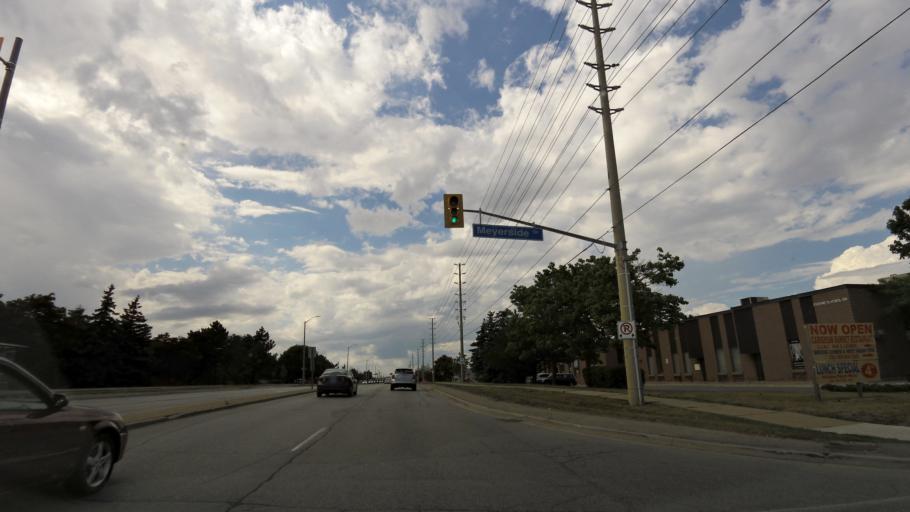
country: CA
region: Ontario
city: Mississauga
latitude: 43.6509
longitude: -79.6649
